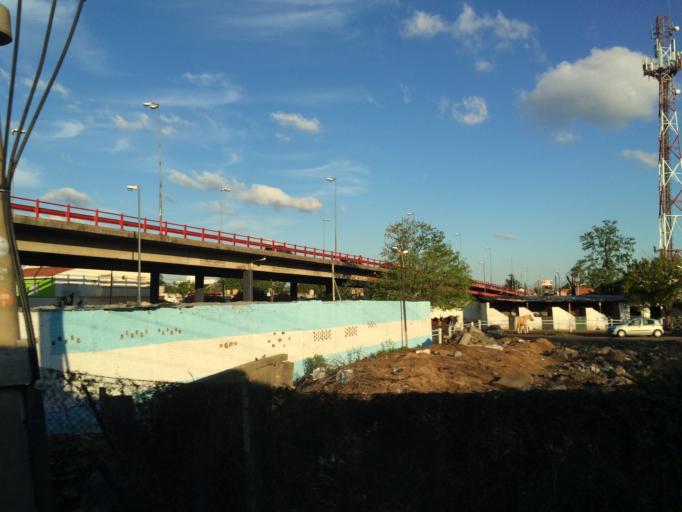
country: AR
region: Buenos Aires
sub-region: Partido de Lanus
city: Lanus
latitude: -34.6951
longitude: -58.3859
